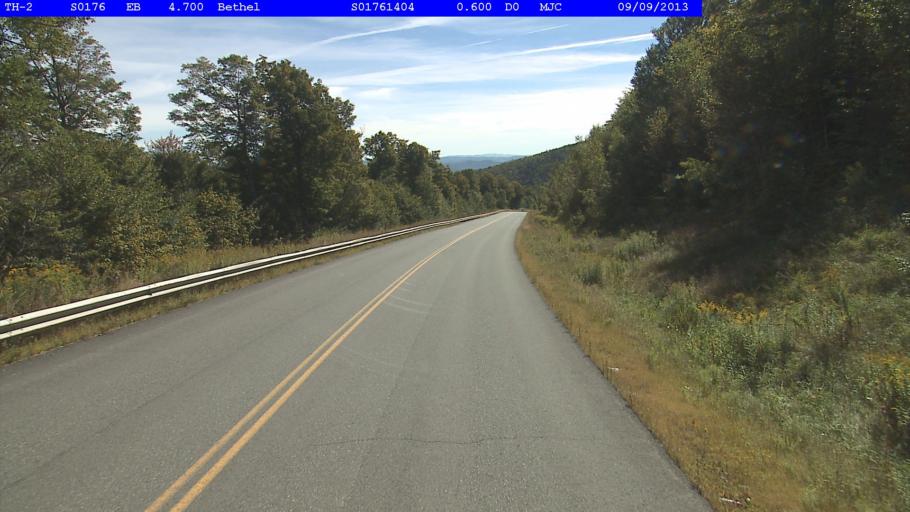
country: US
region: Vermont
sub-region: Orange County
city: Randolph
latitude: 43.8516
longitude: -72.7392
